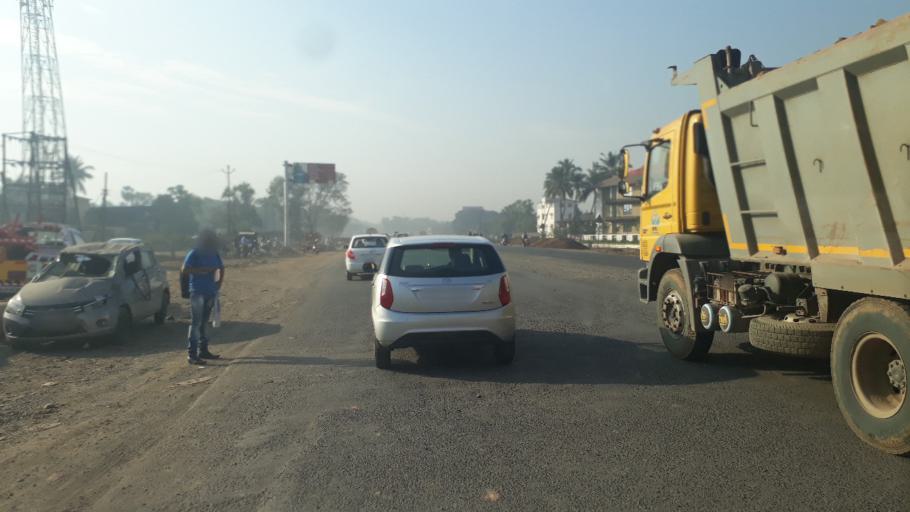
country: IN
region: Maharashtra
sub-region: Raigarh
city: Kalundri
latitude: 18.9676
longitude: 73.1319
